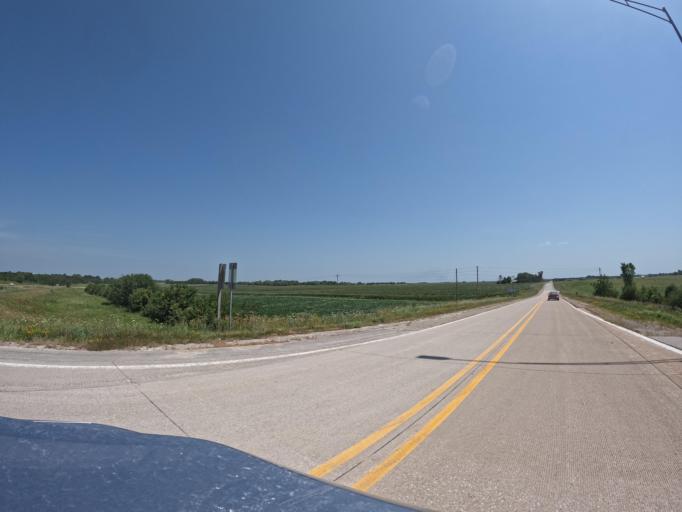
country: US
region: Iowa
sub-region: Henry County
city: Mount Pleasant
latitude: 40.9376
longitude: -91.5315
